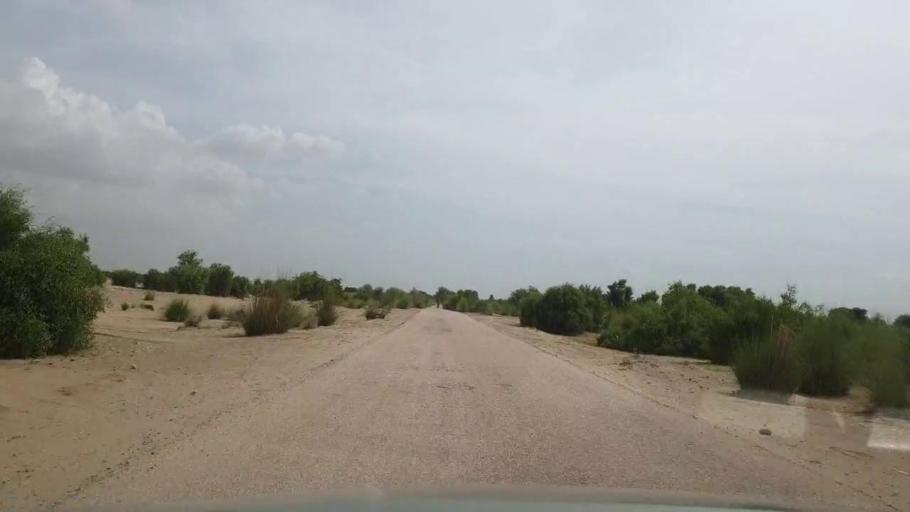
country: PK
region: Sindh
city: Kot Diji
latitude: 27.1225
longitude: 69.0266
